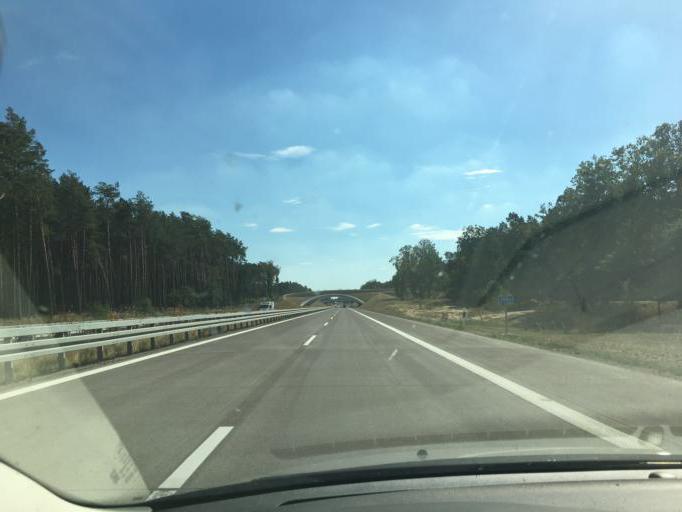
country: DE
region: Mecklenburg-Vorpommern
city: Grabow
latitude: 53.2117
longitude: 11.6443
